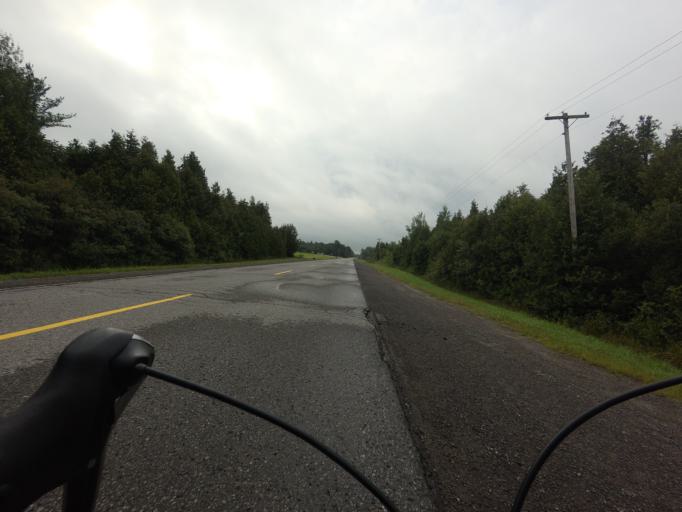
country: CA
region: Ontario
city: Bells Corners
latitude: 45.1555
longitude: -75.7888
